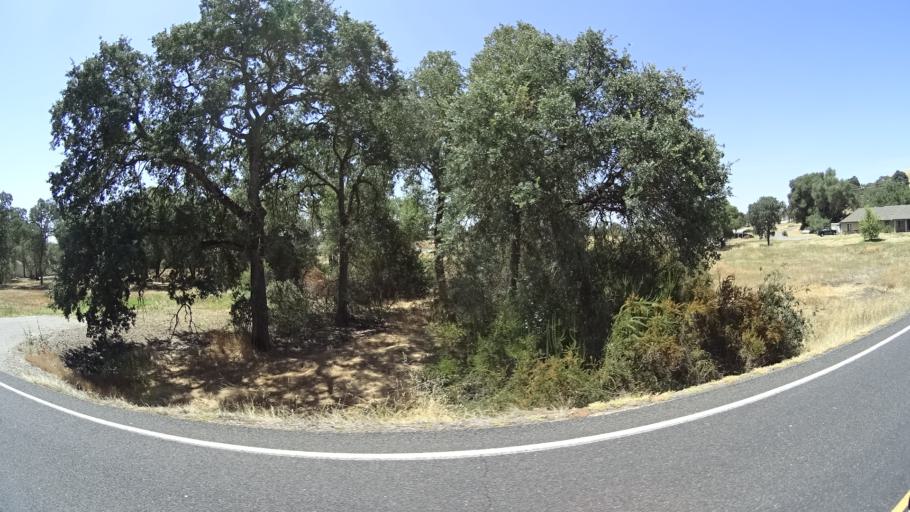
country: US
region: California
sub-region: Calaveras County
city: Rancho Calaveras
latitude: 38.1636
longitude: -120.9532
